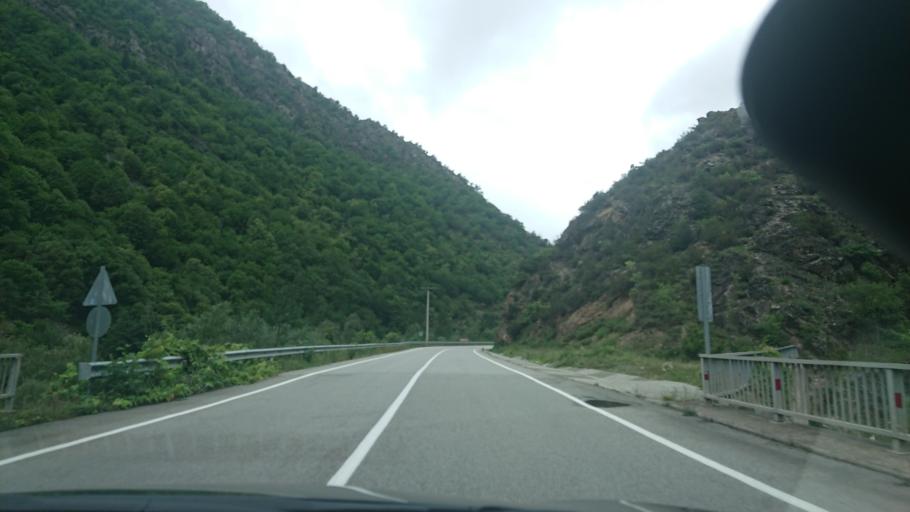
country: TR
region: Gumushane
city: Kurtun
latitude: 40.7318
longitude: 39.0119
